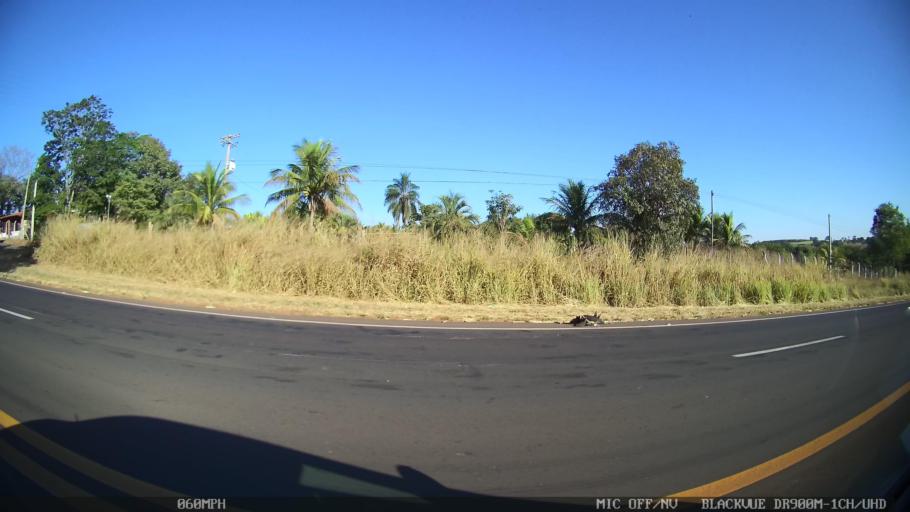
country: BR
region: Sao Paulo
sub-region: Olimpia
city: Olimpia
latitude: -20.7057
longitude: -48.9564
